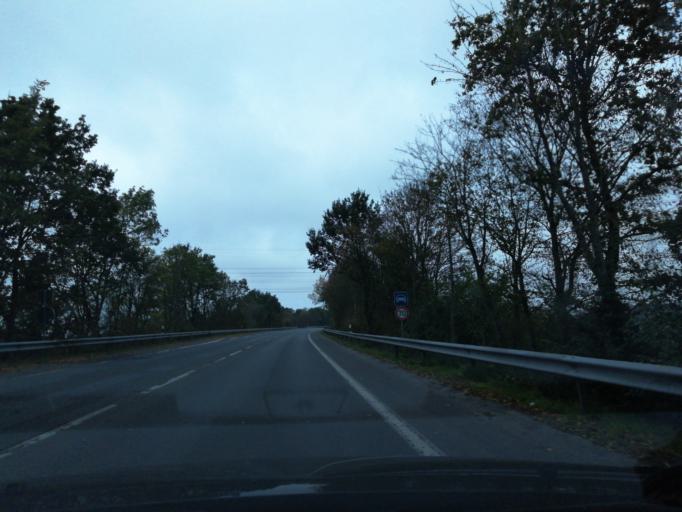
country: DE
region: Lower Saxony
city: Fedderwarden
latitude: 53.5428
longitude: 8.0517
